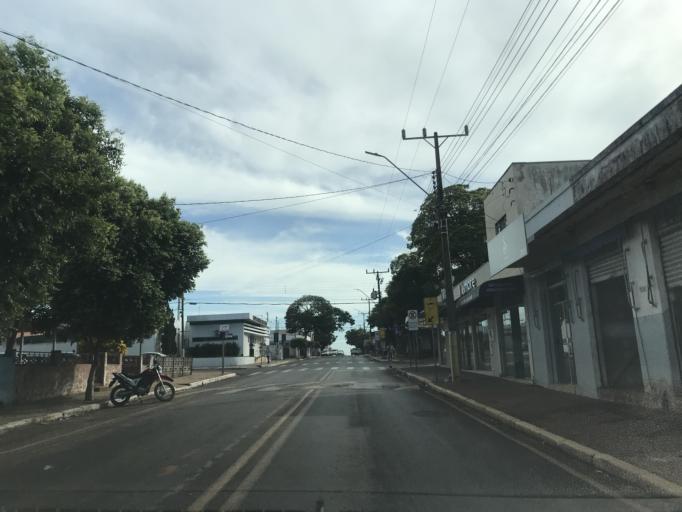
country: BR
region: Parana
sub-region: Paranavai
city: Nova Aurora
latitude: -22.9342
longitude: -52.6859
